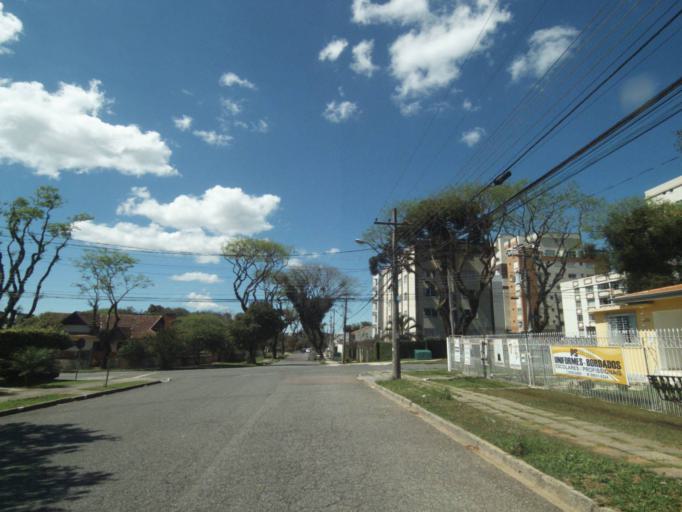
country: BR
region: Parana
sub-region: Curitiba
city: Curitiba
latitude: -25.3955
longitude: -49.2488
